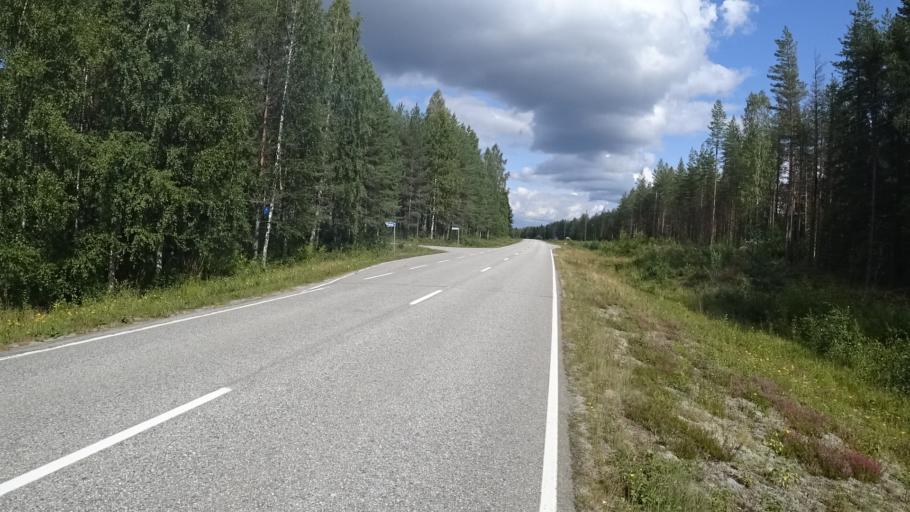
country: FI
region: North Karelia
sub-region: Joensuu
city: Ilomantsi
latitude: 62.6313
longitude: 31.2756
